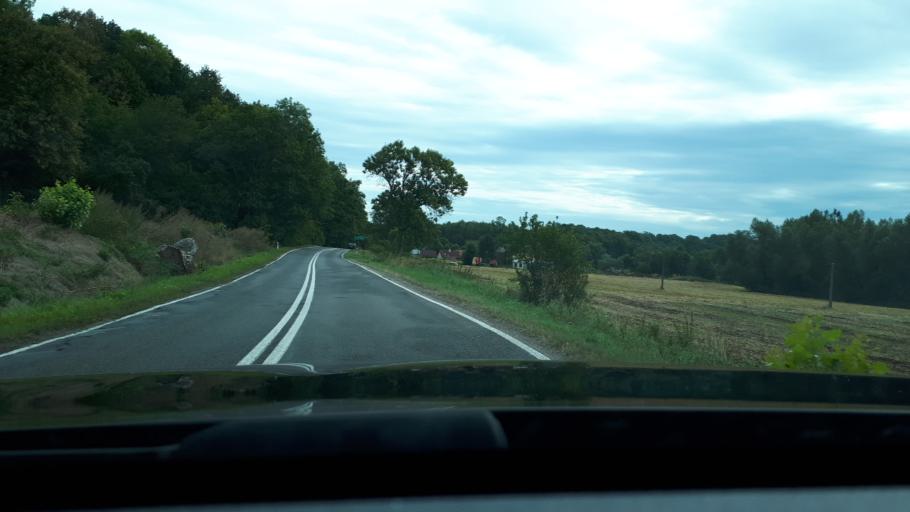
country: PL
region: Lower Silesian Voivodeship
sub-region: Powiat lwowecki
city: Lwowek Slaski
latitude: 51.1001
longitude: 15.5408
